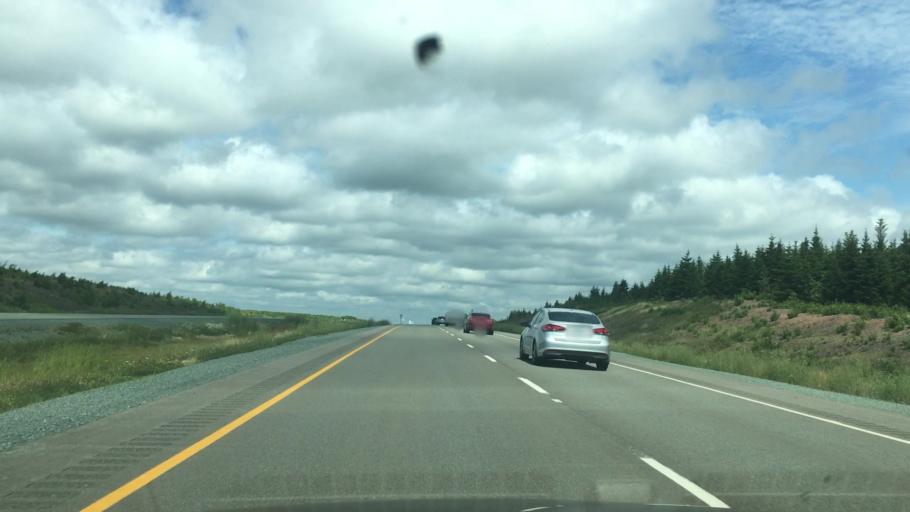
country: CA
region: Nova Scotia
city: Oxford
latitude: 45.6164
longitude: -63.7398
